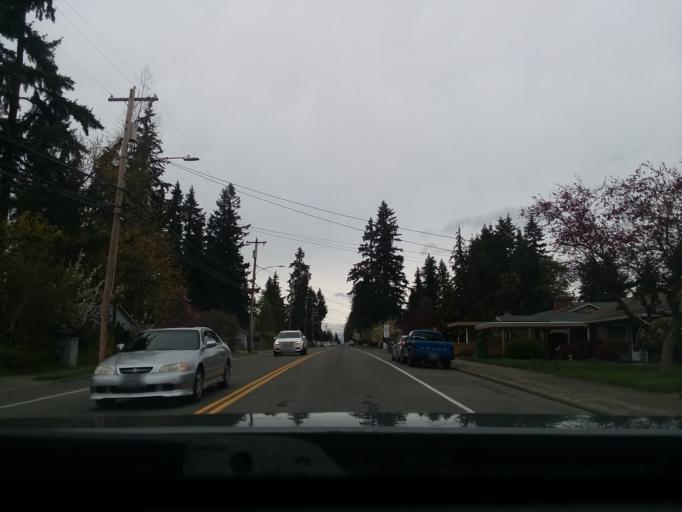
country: US
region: Washington
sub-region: Snohomish County
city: Mountlake Terrace
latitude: 47.7924
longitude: -122.3085
